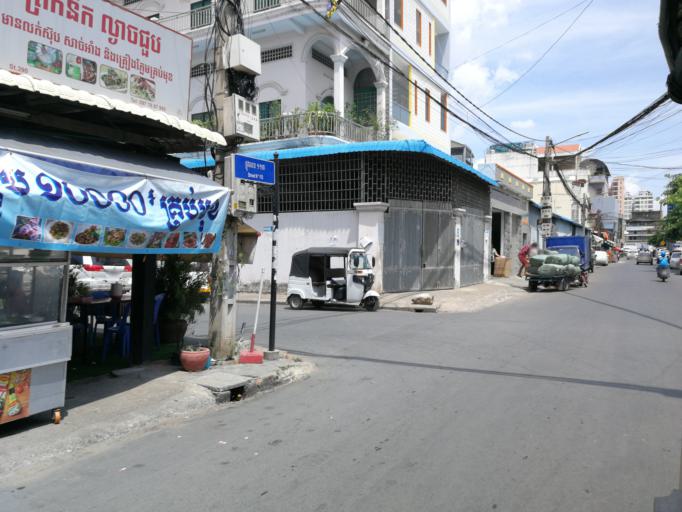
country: KH
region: Phnom Penh
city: Phnom Penh
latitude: 11.5456
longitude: 104.9180
